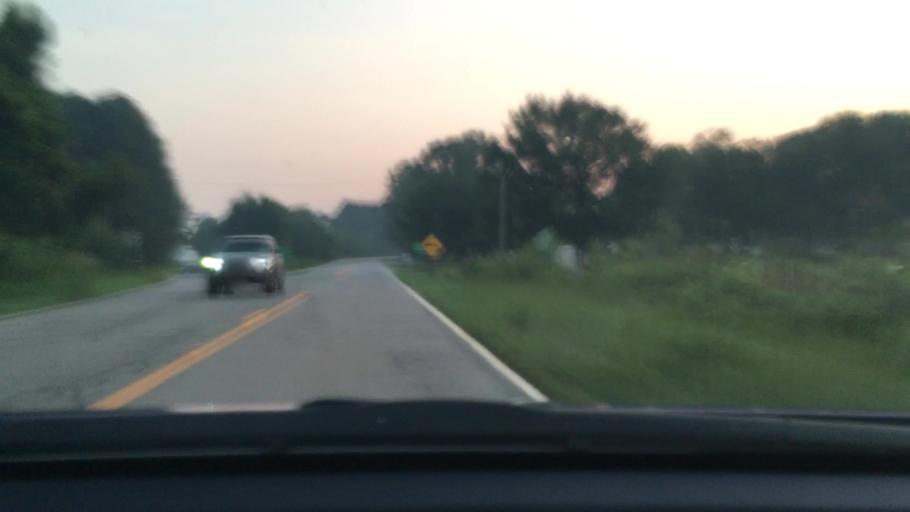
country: US
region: South Carolina
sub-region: Sumter County
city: East Sumter
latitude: 34.0054
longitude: -80.2874
